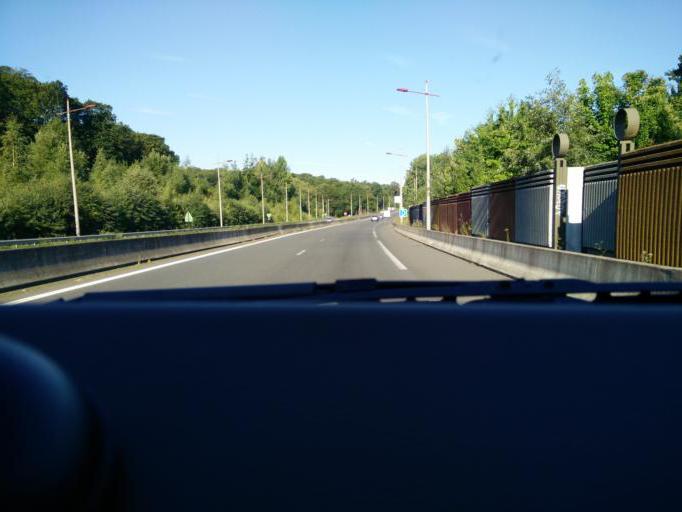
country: FR
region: Nord-Pas-de-Calais
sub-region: Departement du Pas-de-Calais
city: Barlin
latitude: 50.4426
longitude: 2.6108
